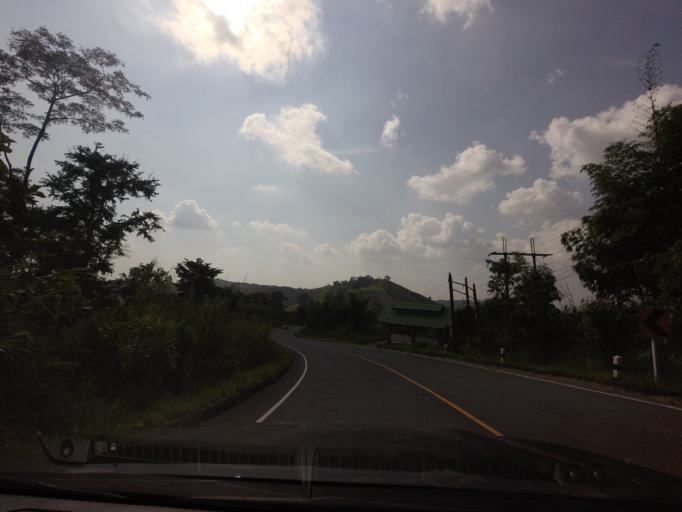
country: TH
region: Nan
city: Santi Suk
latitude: 18.9730
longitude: 100.9858
